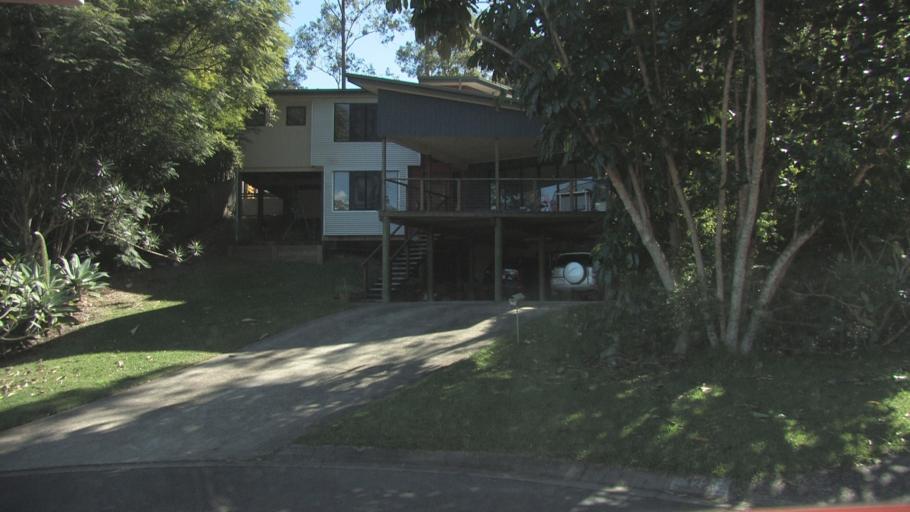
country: AU
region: Queensland
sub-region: Logan
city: Slacks Creek
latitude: -27.6491
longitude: 153.1912
